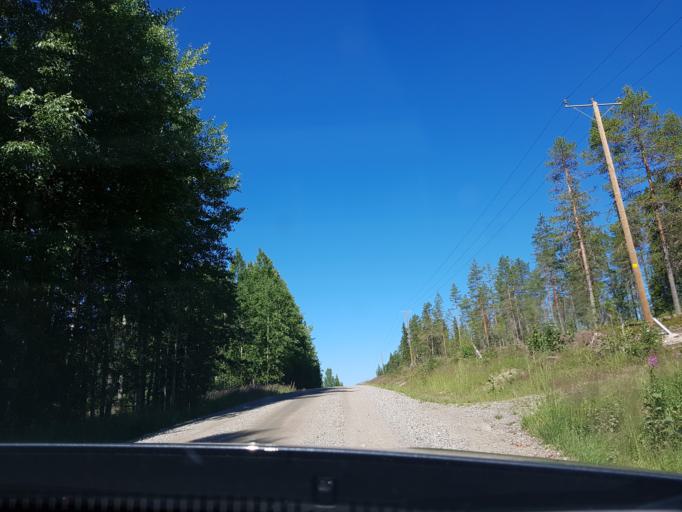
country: FI
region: Kainuu
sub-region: Kehys-Kainuu
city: Kuhmo
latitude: 64.1701
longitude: 29.6438
